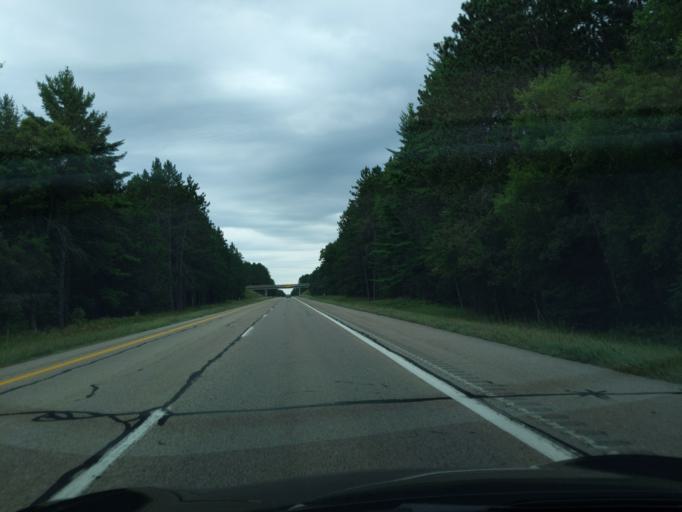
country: US
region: Michigan
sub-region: Roscommon County
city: Houghton Lake
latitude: 44.2055
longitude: -84.7968
